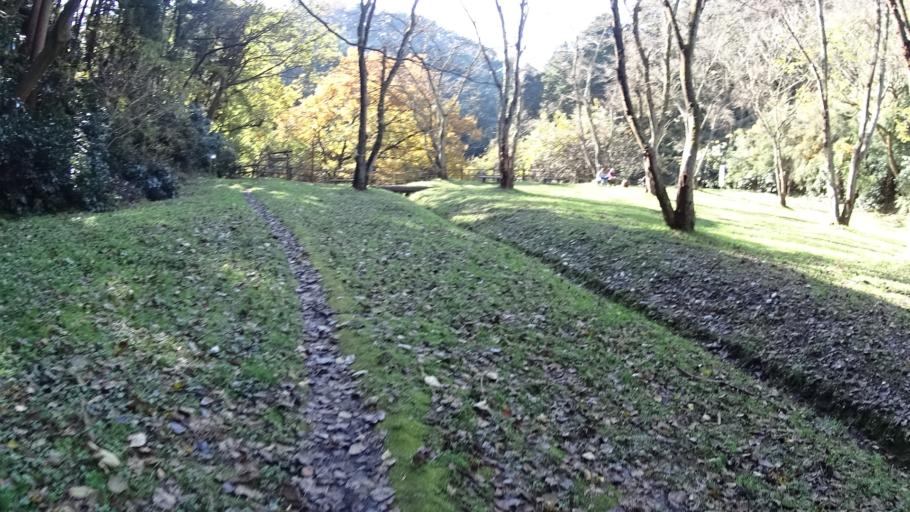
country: JP
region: Kanagawa
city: Kamakura
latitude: 35.3597
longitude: 139.5898
